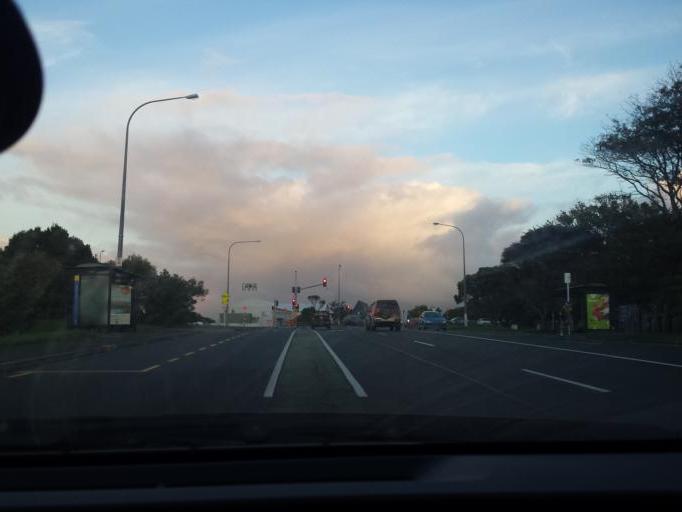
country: NZ
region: Auckland
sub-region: Auckland
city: Tamaki
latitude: -36.8681
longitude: 174.8467
